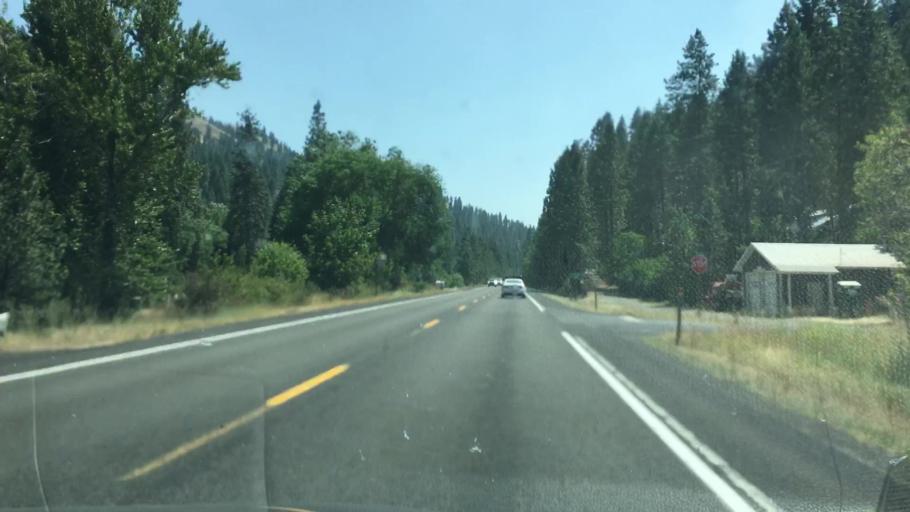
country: US
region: Idaho
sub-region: Valley County
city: McCall
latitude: 45.2551
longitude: -116.3366
